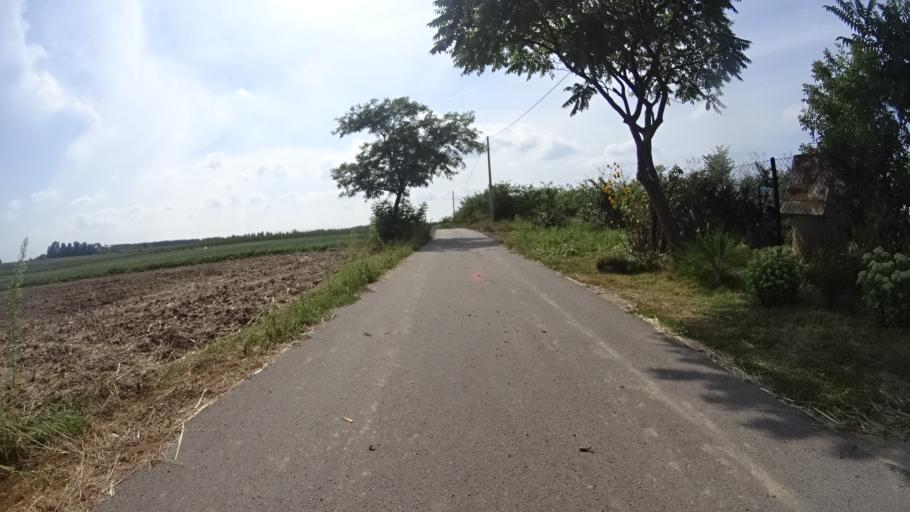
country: PL
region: Masovian Voivodeship
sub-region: Powiat grojecki
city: Goszczyn
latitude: 51.6958
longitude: 20.8414
